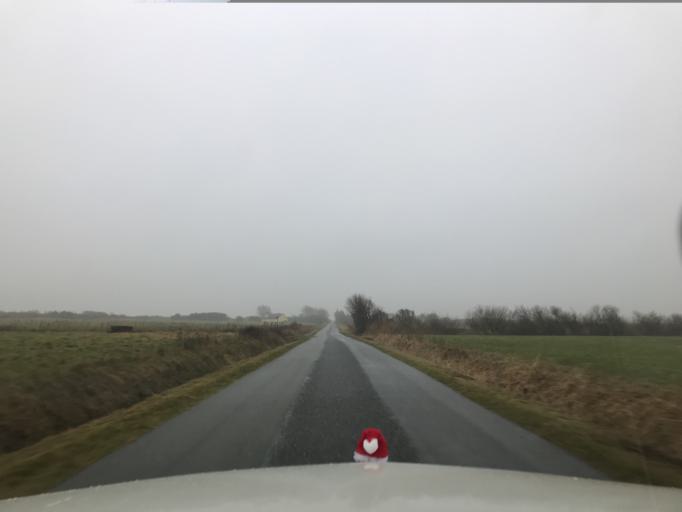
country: DK
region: South Denmark
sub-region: Esbjerg Kommune
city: Tjaereborg
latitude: 55.2842
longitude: 8.5553
